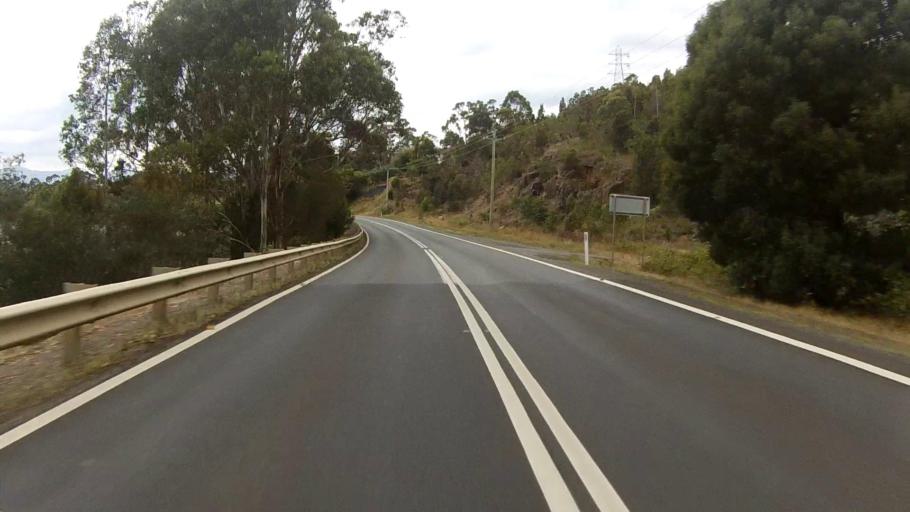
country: AU
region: Tasmania
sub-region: Huon Valley
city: Huonville
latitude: -43.0412
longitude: 147.0548
